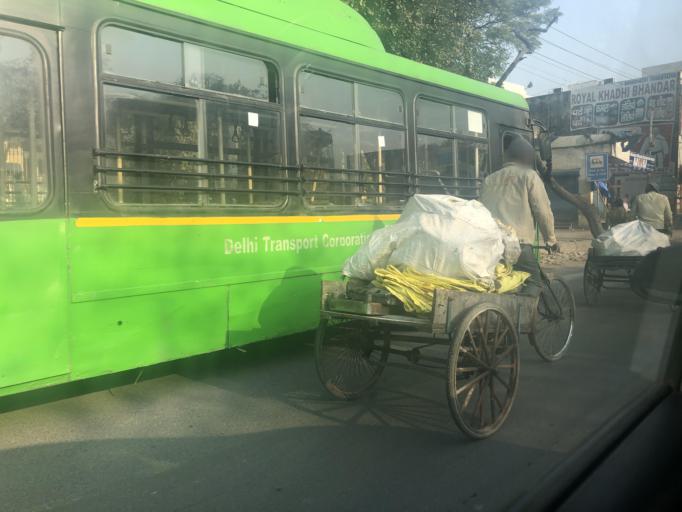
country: IN
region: Haryana
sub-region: Jhajjar
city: Bahadurgarh
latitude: 28.6191
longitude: 76.9744
